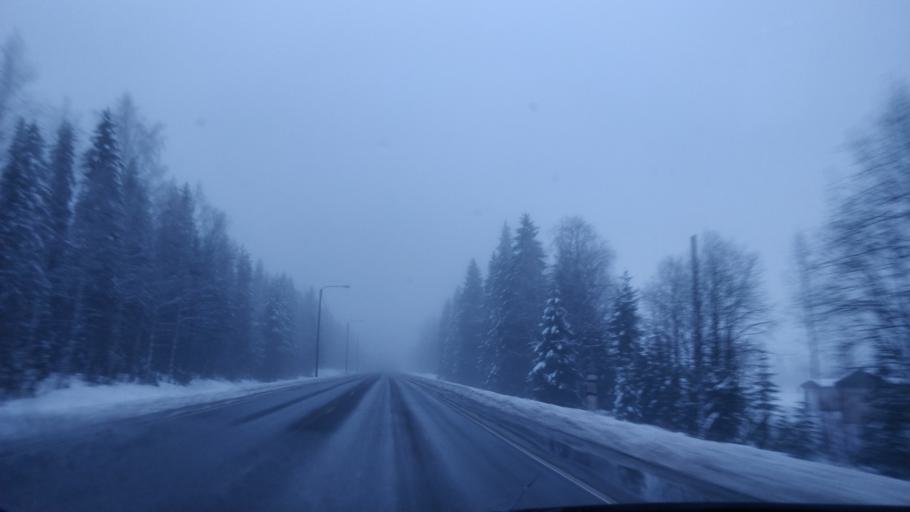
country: FI
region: Lapland
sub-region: Kemi-Tornio
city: Tervola
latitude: 66.1309
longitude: 24.8962
